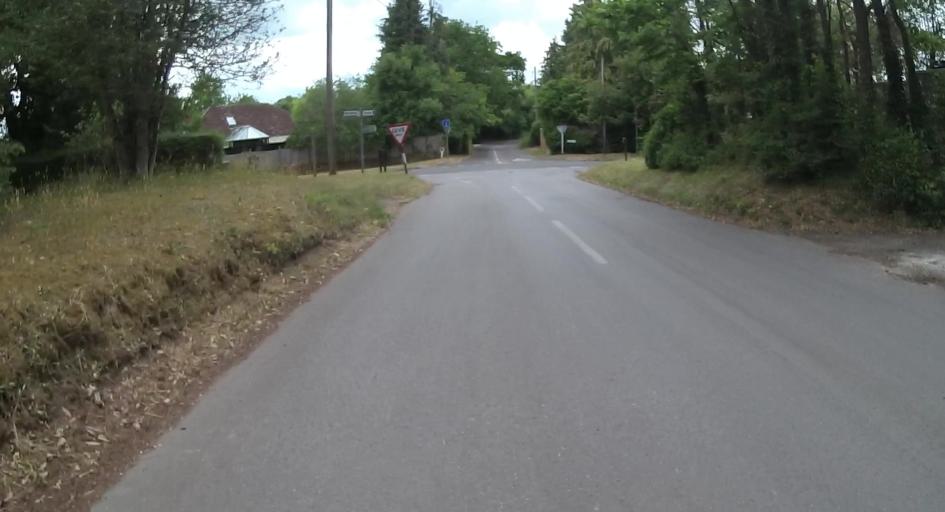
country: GB
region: England
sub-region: Surrey
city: Seale
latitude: 51.2217
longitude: -0.7335
